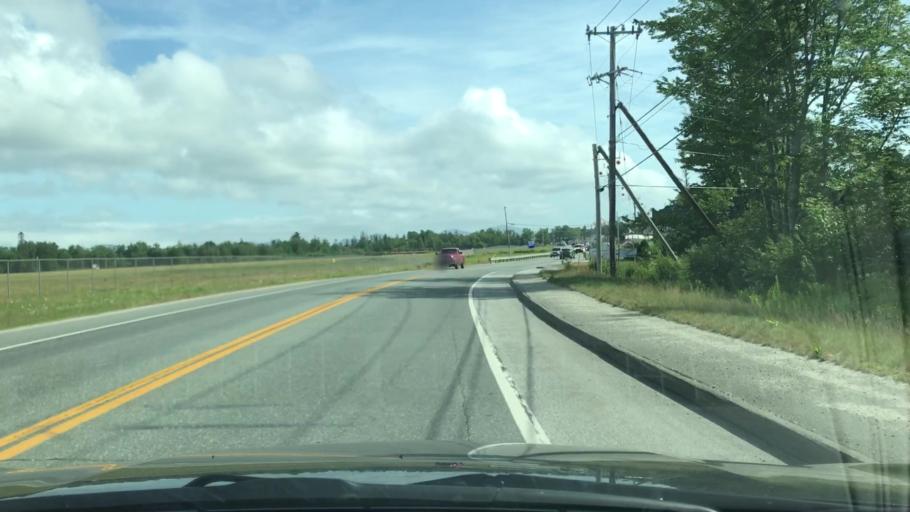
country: US
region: Maine
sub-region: Hancock County
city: Trenton
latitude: 44.4459
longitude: -68.3695
